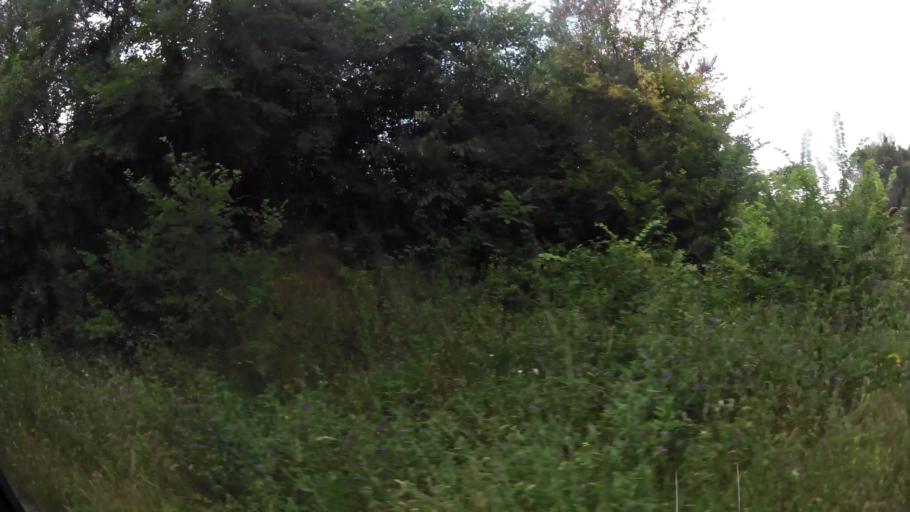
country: GR
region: West Macedonia
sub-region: Nomos Kozanis
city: Kozani
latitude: 40.2967
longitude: 21.8036
